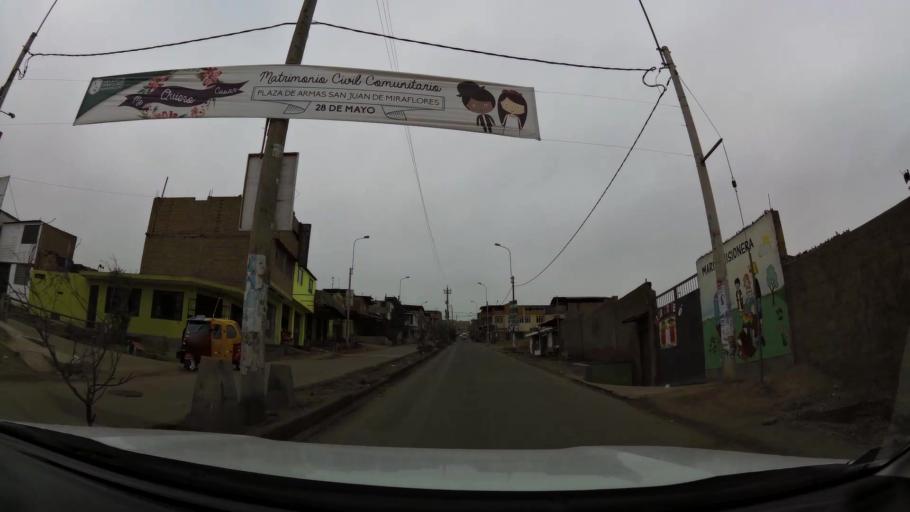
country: PE
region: Lima
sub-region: Lima
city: Surco
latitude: -12.1783
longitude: -76.9605
